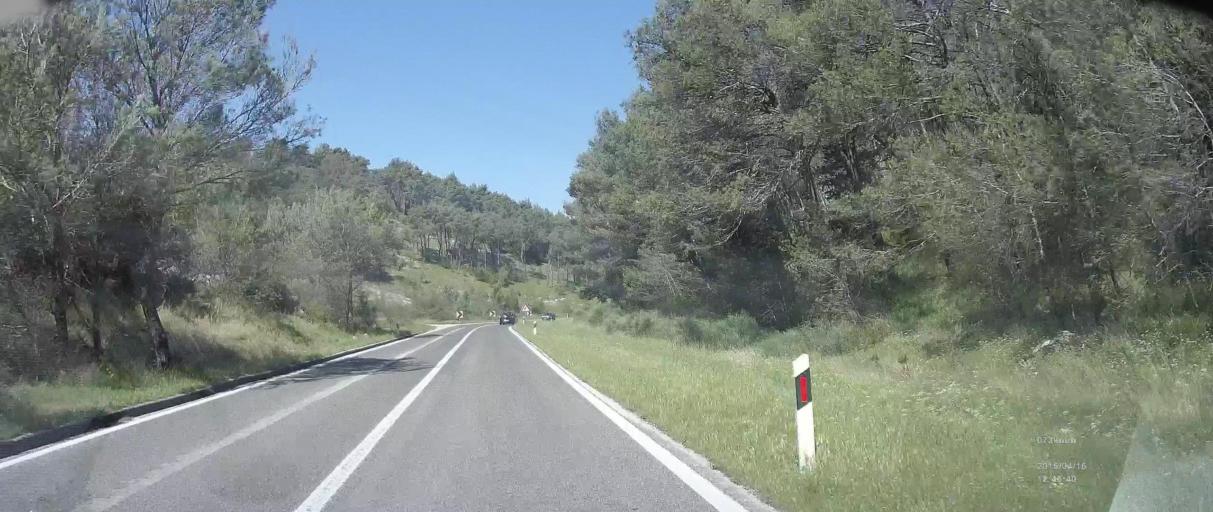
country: HR
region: Sibensko-Kniniska
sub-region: Grad Sibenik
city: Brodarica
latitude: 43.6569
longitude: 16.0517
